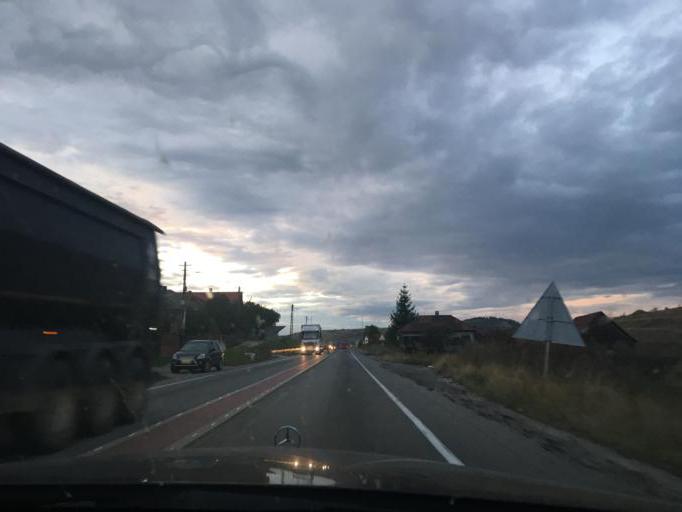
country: RO
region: Cluj
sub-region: Comuna Aghiresu
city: Aghiresu
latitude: 46.8150
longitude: 23.1800
